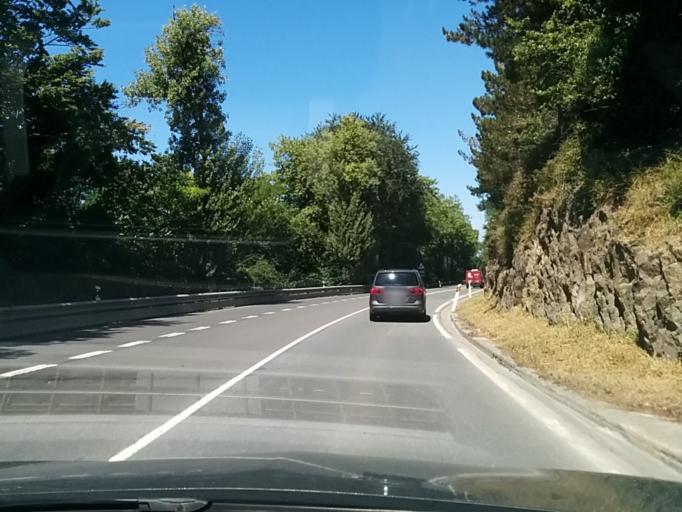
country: ES
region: Basque Country
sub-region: Provincia de Guipuzcoa
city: Orio
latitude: 43.2742
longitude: -2.1395
